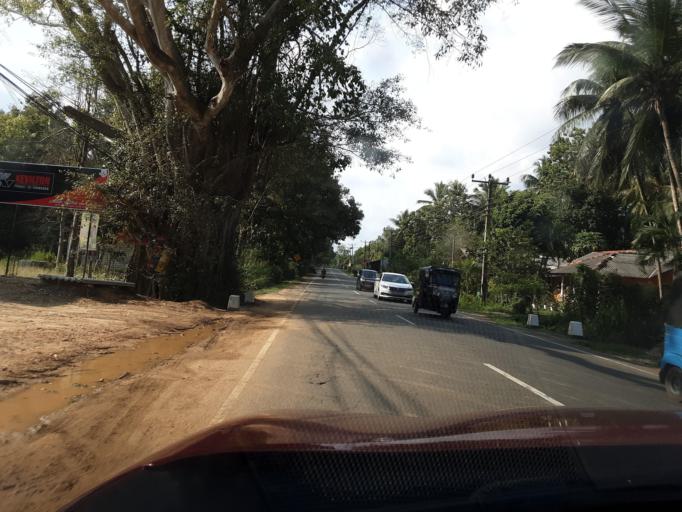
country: LK
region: Uva
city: Haputale
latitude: 6.6724
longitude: 81.1125
